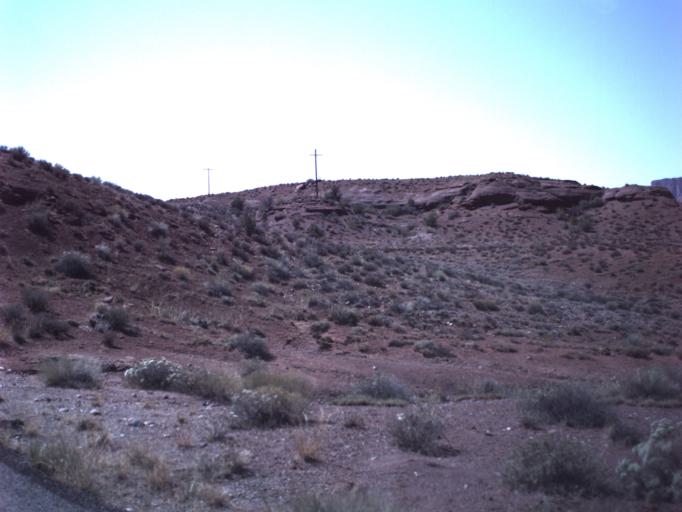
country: US
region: Utah
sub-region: Grand County
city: Moab
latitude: 38.7441
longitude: -109.3310
